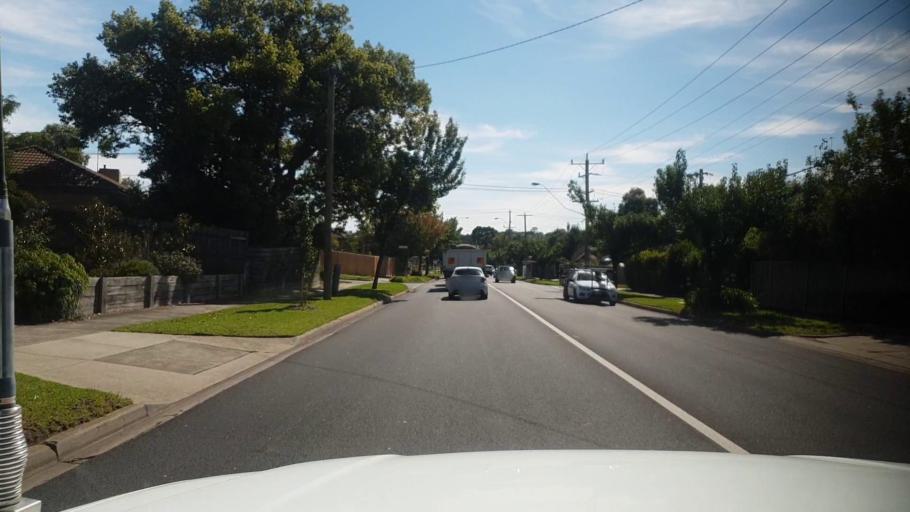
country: AU
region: Victoria
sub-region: Whitehorse
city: Blackburn North
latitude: -37.8046
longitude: 145.1414
